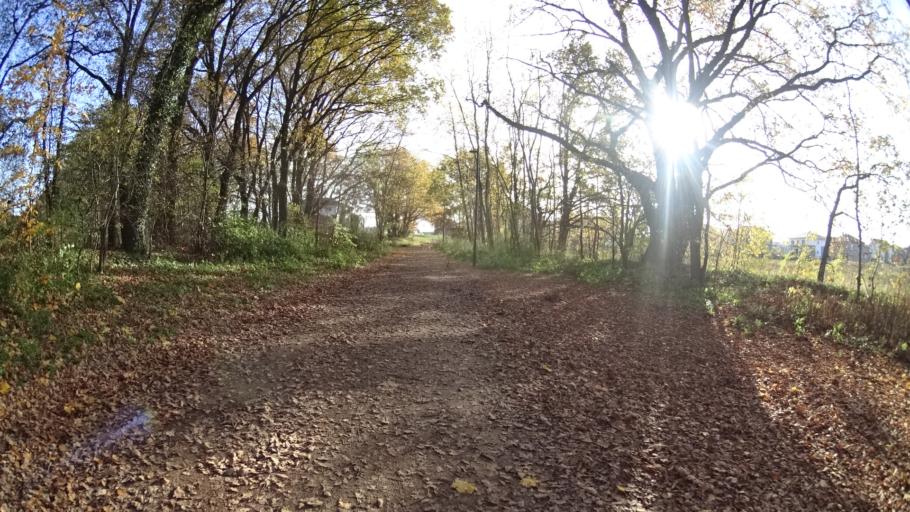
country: DE
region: Lower Saxony
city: Lueneburg
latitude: 53.2571
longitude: 10.4334
